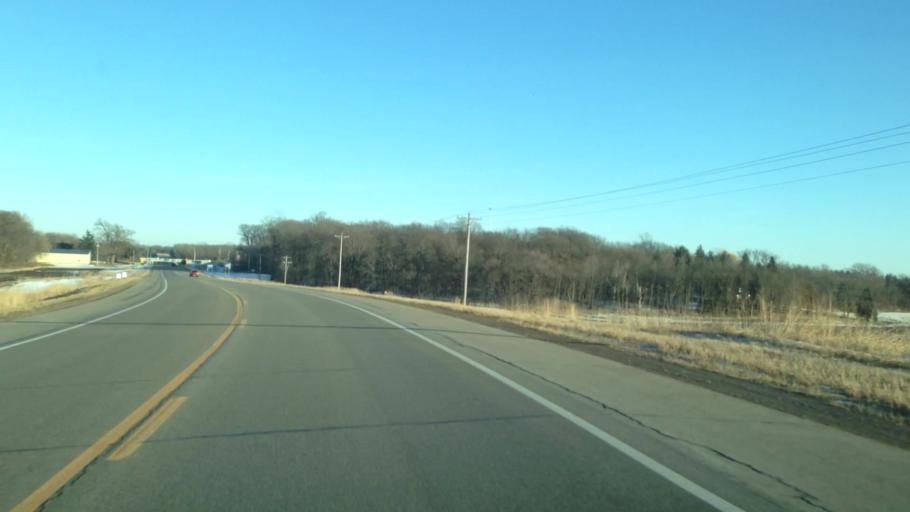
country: US
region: Minnesota
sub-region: Scott County
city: Elko New Market
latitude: 44.4718
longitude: -93.3039
